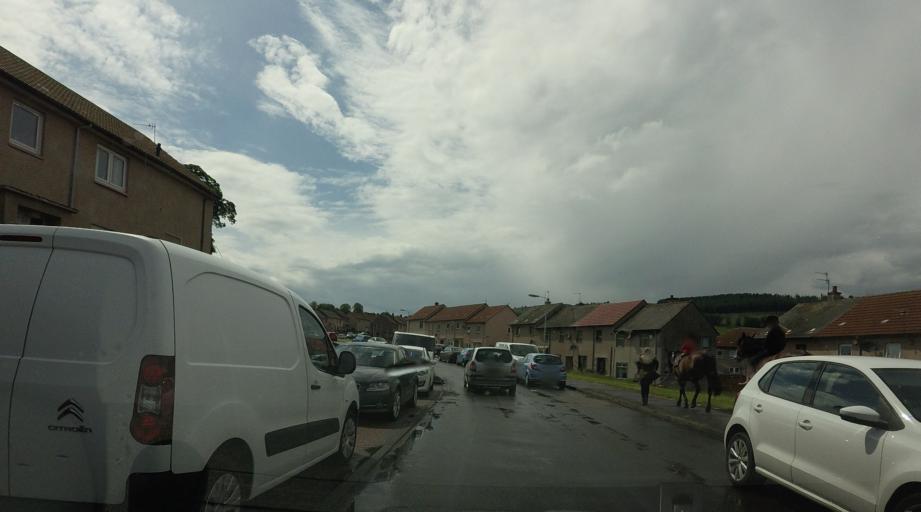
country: GB
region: Scotland
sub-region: Fife
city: Ballingry
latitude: 56.1623
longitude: -3.3241
